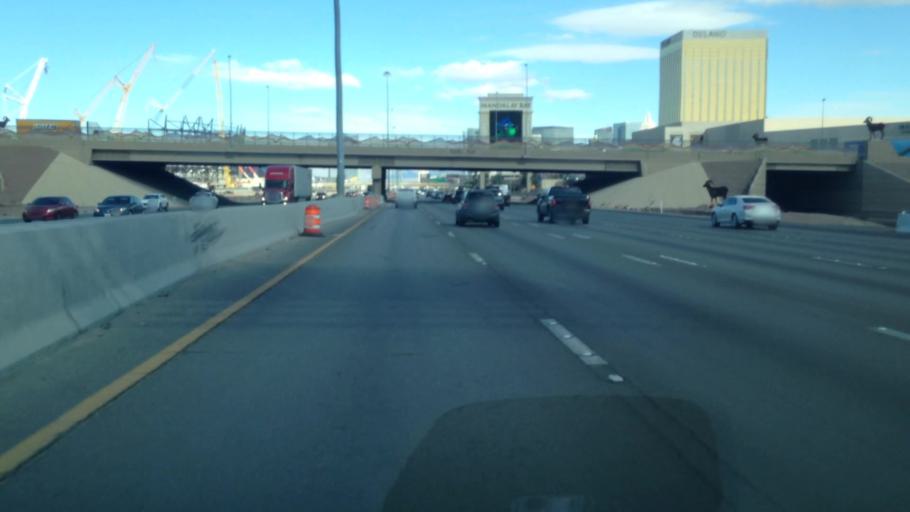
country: US
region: Nevada
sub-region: Clark County
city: Paradise
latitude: 36.0846
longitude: -115.1807
